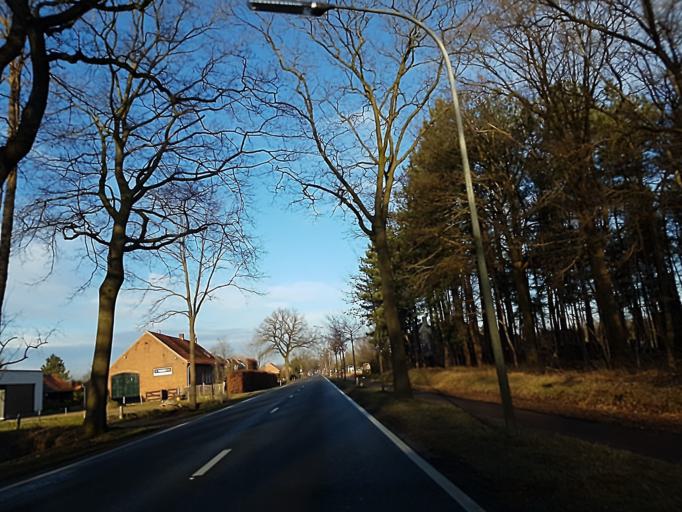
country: BE
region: Flanders
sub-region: Provincie Antwerpen
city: Ravels
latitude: 51.4338
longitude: 5.0247
